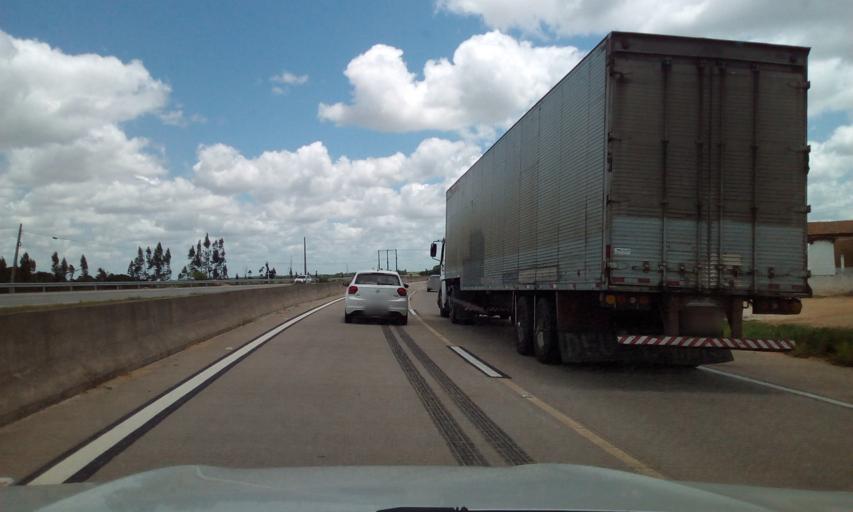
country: BR
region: Alagoas
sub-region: Junqueiro
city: Junqueiro
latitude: -9.8975
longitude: -36.4599
